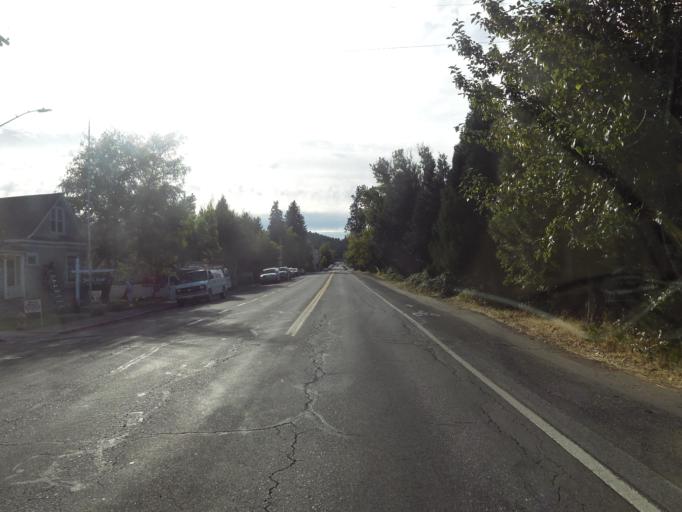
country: US
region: California
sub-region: Siskiyou County
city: Mount Shasta
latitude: 41.3171
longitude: -122.3173
